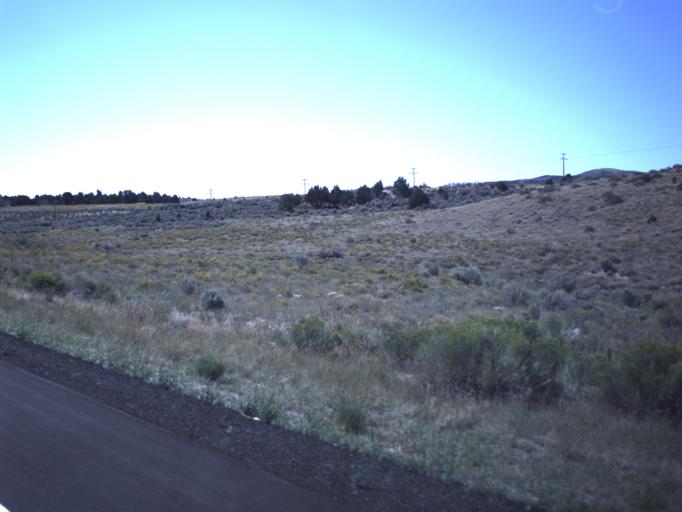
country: US
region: Utah
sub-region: Utah County
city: Genola
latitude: 39.9784
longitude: -112.2602
